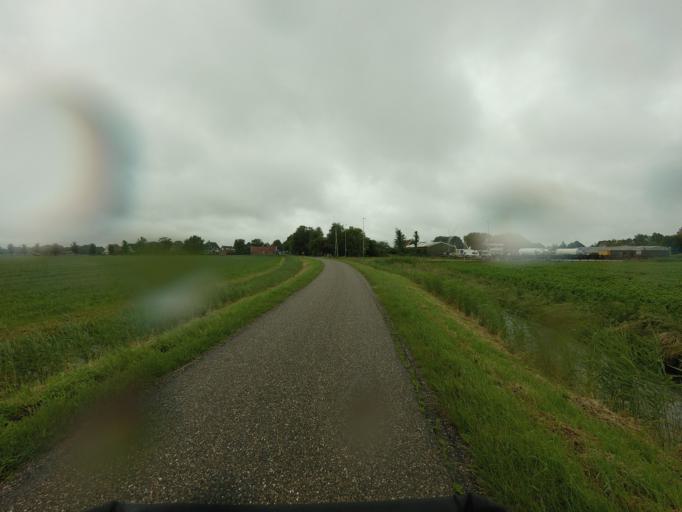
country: NL
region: North Holland
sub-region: Gemeente Opmeer
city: Opmeer
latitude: 52.7481
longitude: 4.9582
